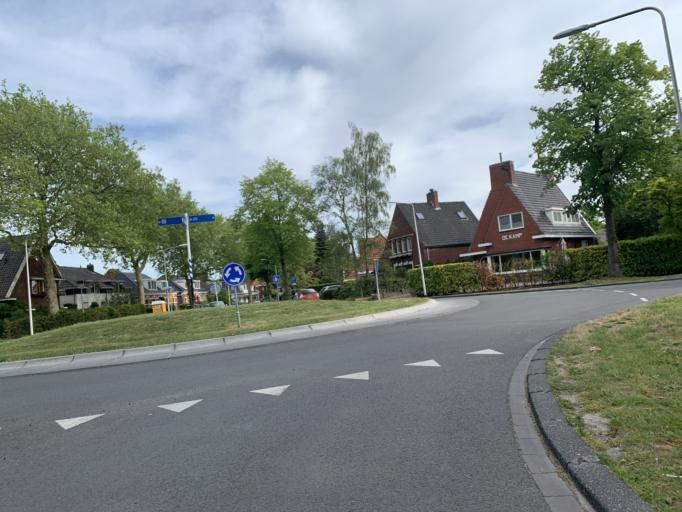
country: NL
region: Groningen
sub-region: Gemeente Haren
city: Haren
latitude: 53.1755
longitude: 6.6077
